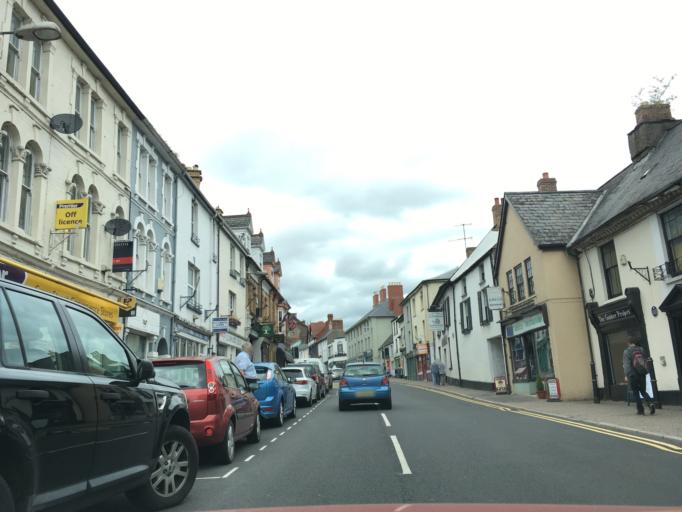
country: GB
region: Wales
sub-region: Monmouthshire
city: Abergavenny
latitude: 51.8203
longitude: -3.0164
